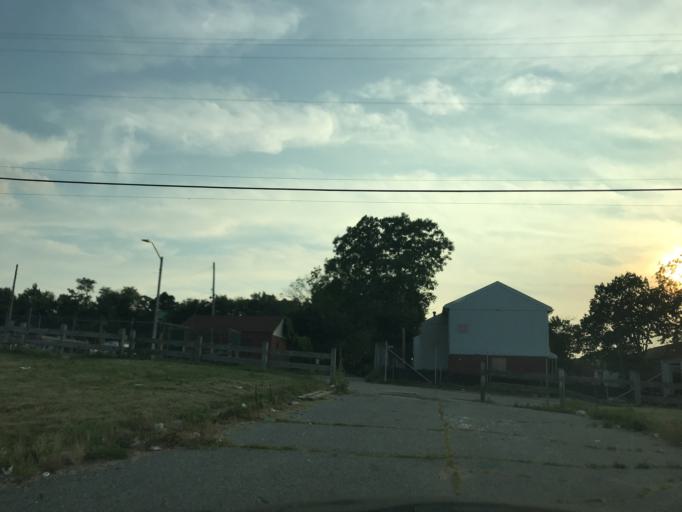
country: US
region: Maryland
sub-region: Baltimore County
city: Dundalk
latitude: 39.2805
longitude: -76.5401
